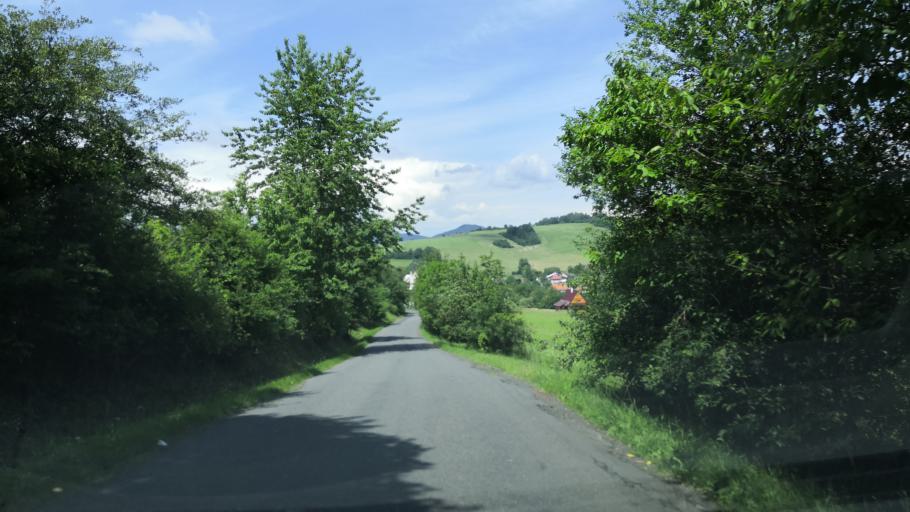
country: CZ
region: Zlin
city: Vidce
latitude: 49.4372
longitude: 18.0938
